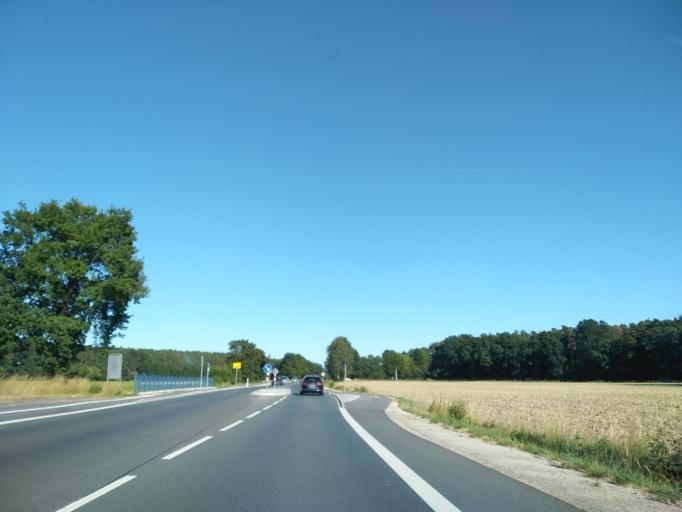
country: DE
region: Bavaria
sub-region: Regierungsbezirk Mittelfranken
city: Hessdorf
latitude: 49.6254
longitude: 10.9415
